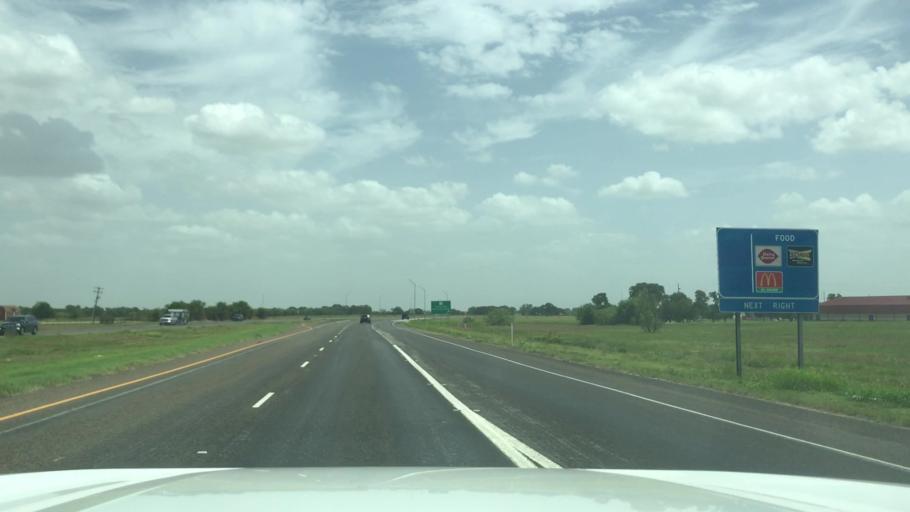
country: US
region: Texas
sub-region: Falls County
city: Marlin
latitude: 31.3173
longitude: -96.8790
